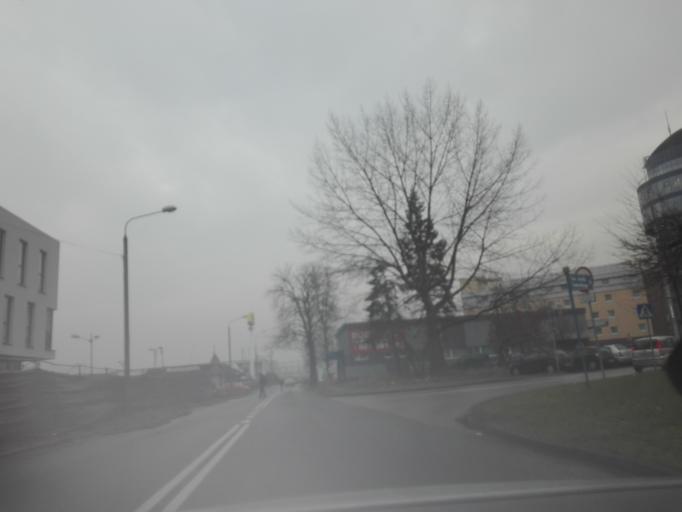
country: PL
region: Silesian Voivodeship
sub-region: Katowice
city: Katowice
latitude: 50.2464
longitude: 19.0371
